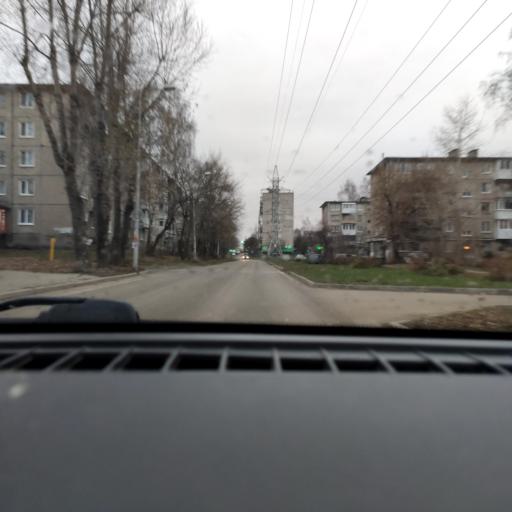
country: RU
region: Perm
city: Perm
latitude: 57.9814
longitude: 56.2115
